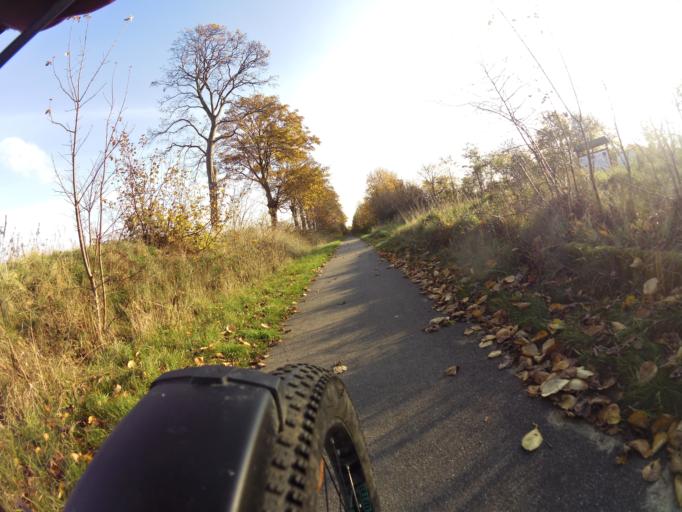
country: PL
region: Pomeranian Voivodeship
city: Strzelno
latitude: 54.7661
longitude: 18.2452
